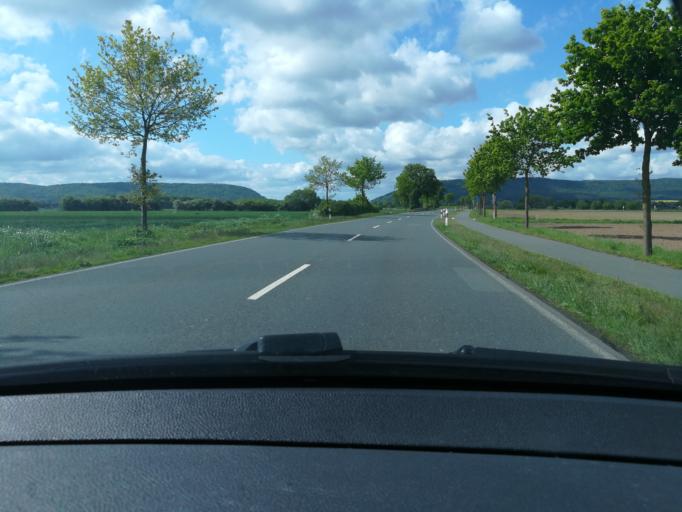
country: DE
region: North Rhine-Westphalia
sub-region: Regierungsbezirk Detmold
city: Minden
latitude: 52.2817
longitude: 8.9295
